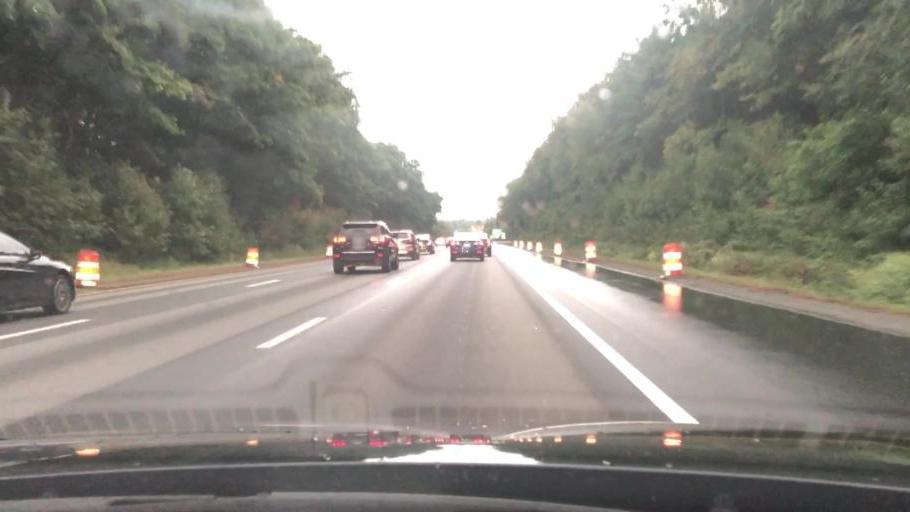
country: US
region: Massachusetts
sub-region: Middlesex County
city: Tewksbury
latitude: 42.6472
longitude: -71.2209
